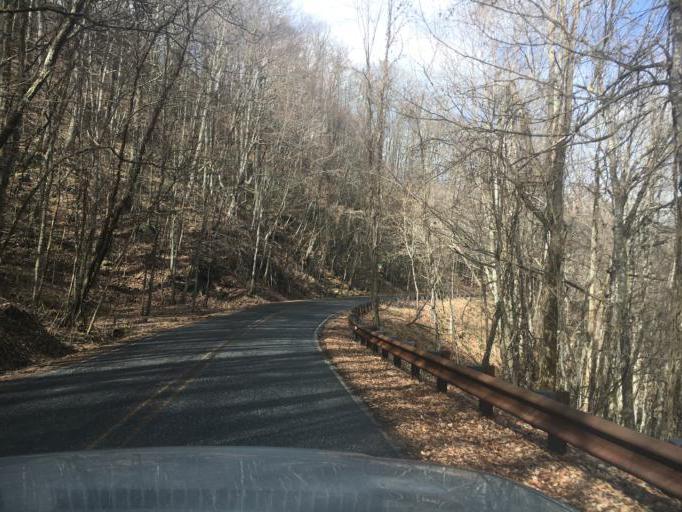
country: US
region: North Carolina
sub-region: Transylvania County
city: Brevard
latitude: 35.3692
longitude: -82.8040
